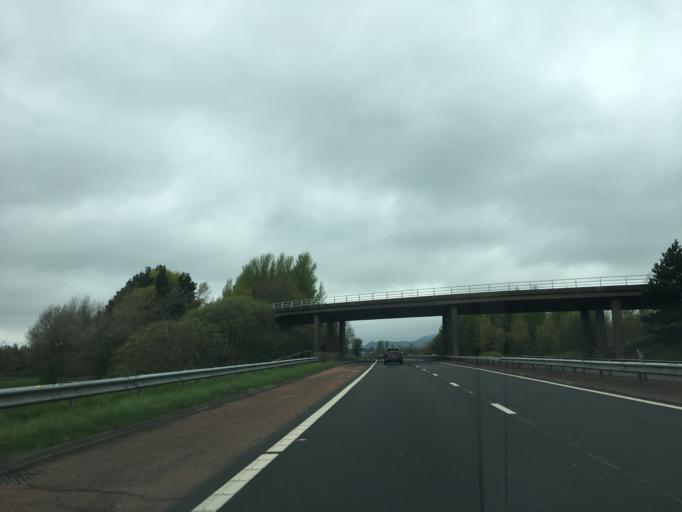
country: GB
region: Scotland
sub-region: Renfrewshire
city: Bishopton
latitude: 55.8995
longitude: -4.4842
